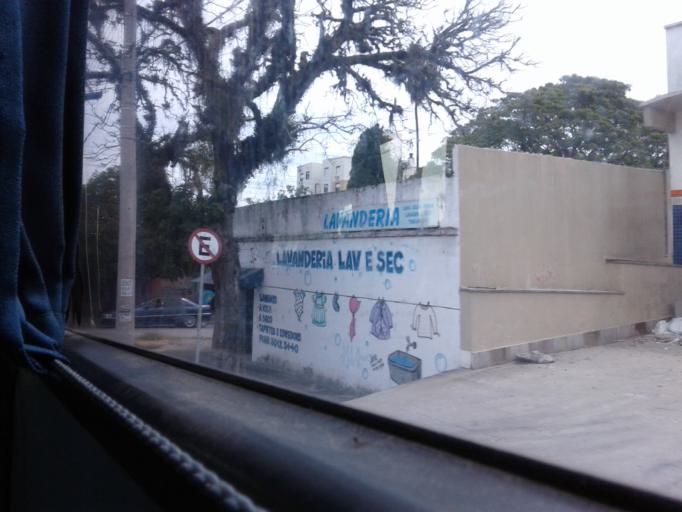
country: BR
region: Rio Grande do Sul
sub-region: Porto Alegre
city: Porto Alegre
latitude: -30.0947
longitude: -51.2293
